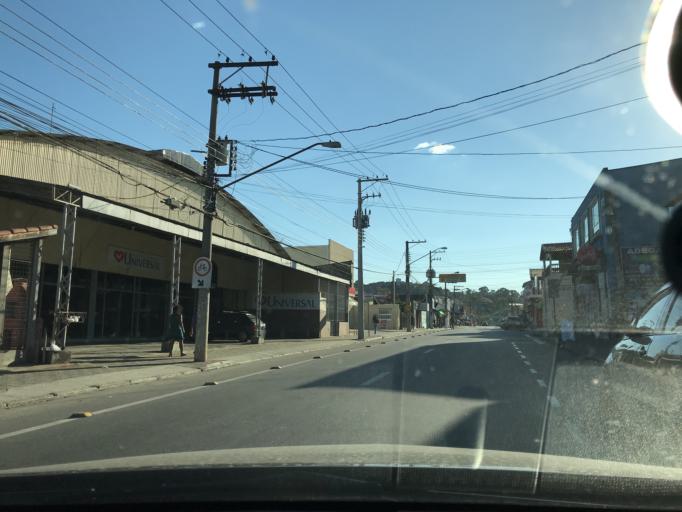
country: BR
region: Sao Paulo
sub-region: Sao Jose Dos Campos
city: Sao Jose dos Campos
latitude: -23.1522
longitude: -45.9008
